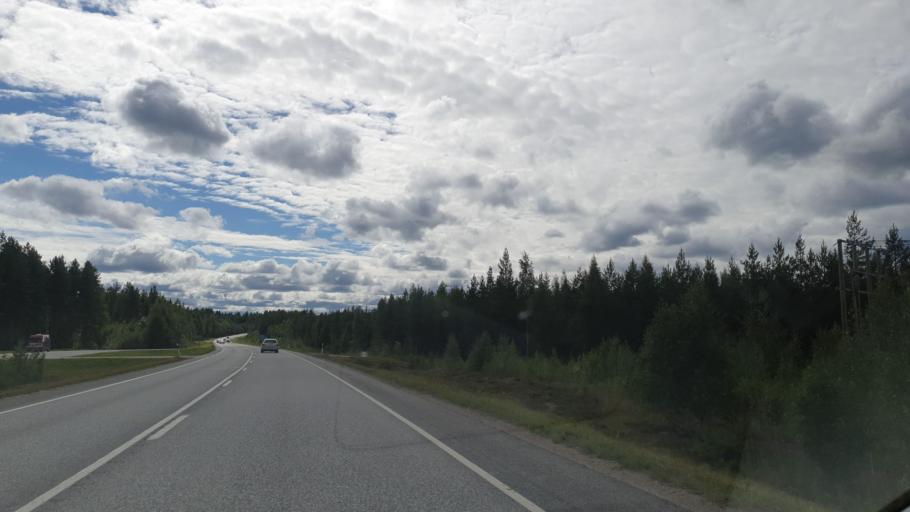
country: FI
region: Kainuu
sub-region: Kajaani
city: Kajaani
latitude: 64.1892
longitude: 27.6030
